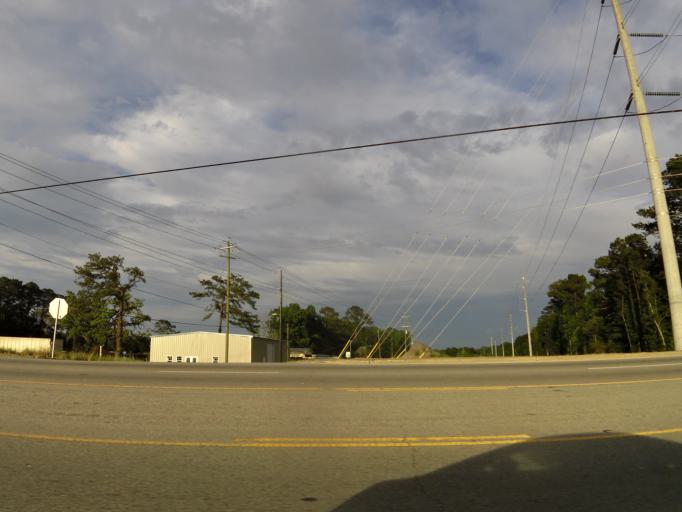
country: US
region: Georgia
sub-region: Chatham County
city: Garden City
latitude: 32.0824
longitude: -81.1957
